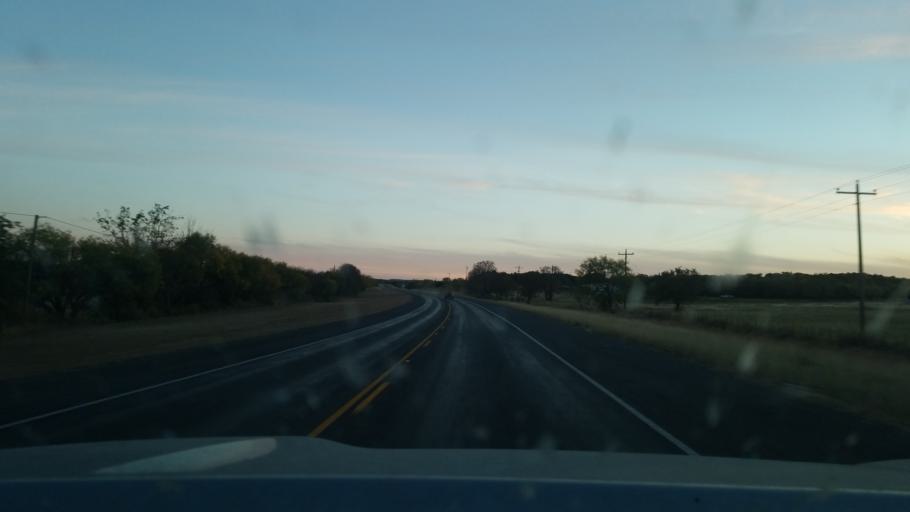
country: US
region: Texas
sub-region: Stephens County
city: Breckenridge
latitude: 32.5984
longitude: -98.8994
